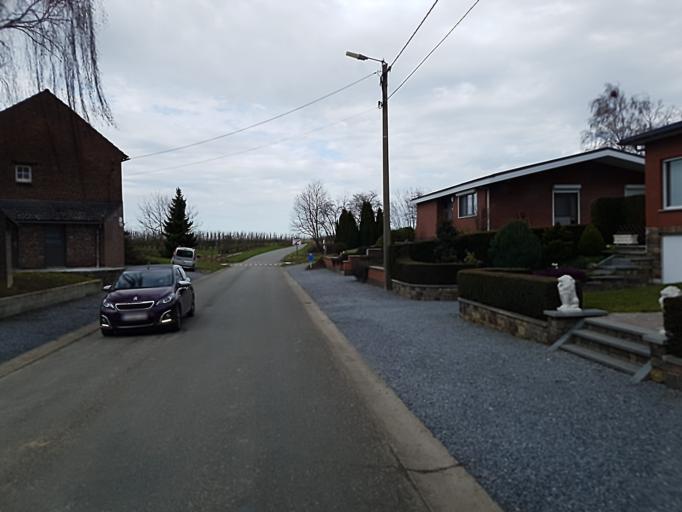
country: BE
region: Flanders
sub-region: Provincie Limburg
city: Heers
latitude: 50.8121
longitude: 5.2618
